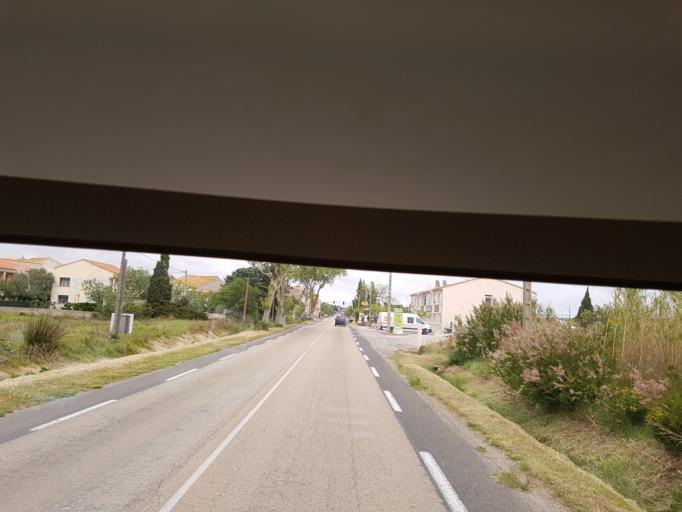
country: FR
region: Languedoc-Roussillon
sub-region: Departement de l'Aude
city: Leucate
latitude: 42.8923
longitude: 2.9963
